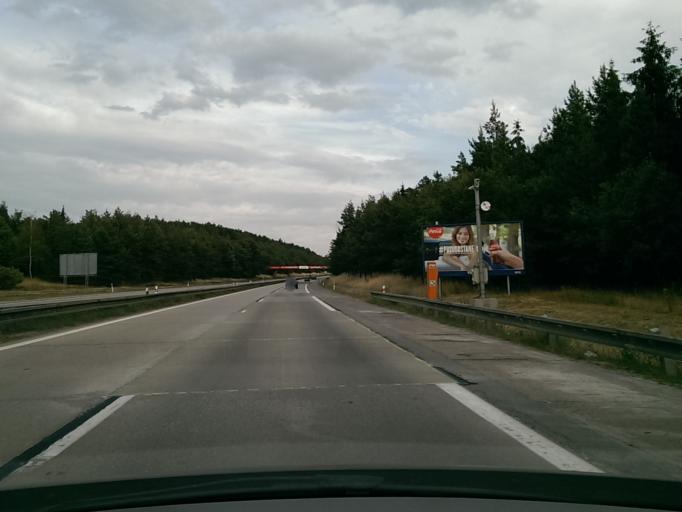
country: CZ
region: Vysocina
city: Krizanov
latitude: 49.3170
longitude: 16.0982
